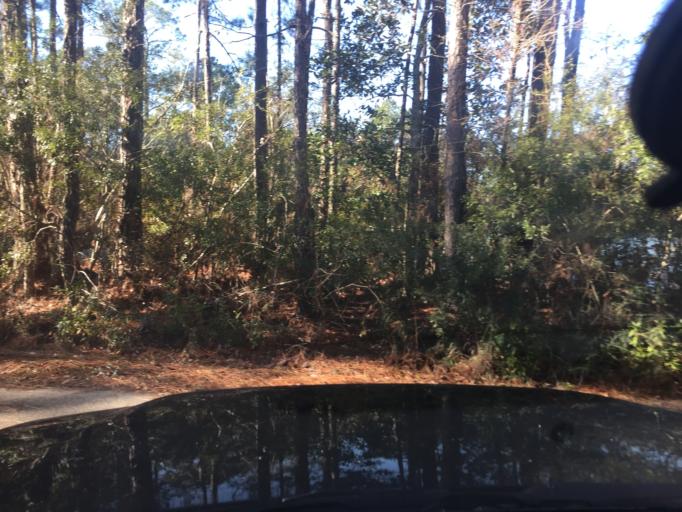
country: US
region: Louisiana
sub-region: Saint Tammany Parish
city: Slidell
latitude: 30.3064
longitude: -89.7377
